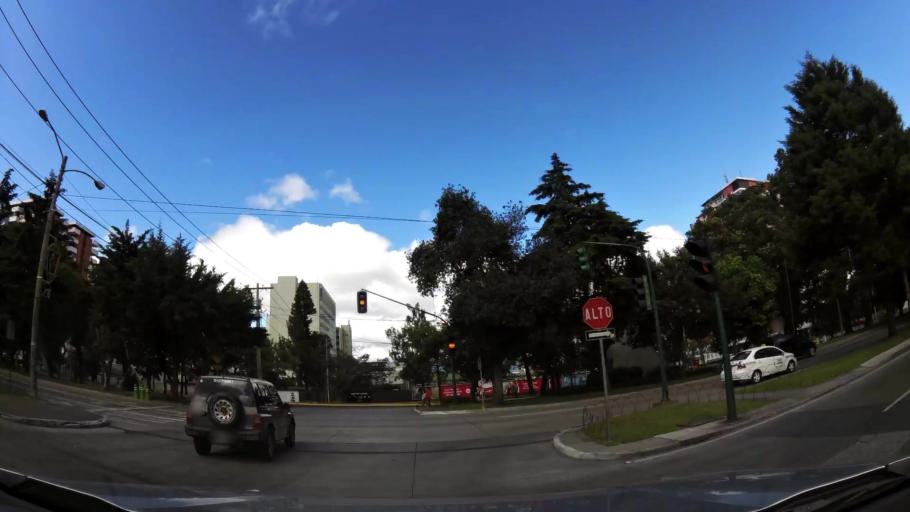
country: GT
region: Guatemala
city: Santa Catarina Pinula
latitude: 14.5971
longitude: -90.5169
